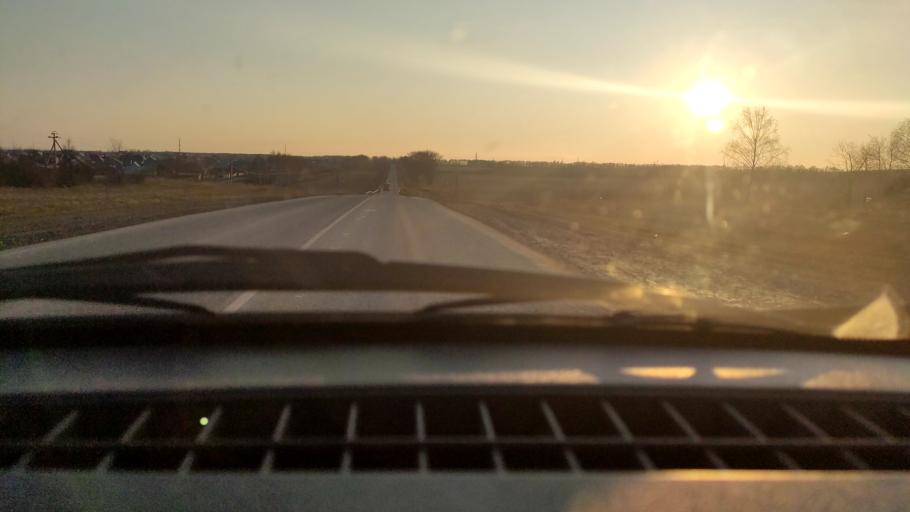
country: RU
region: Bashkortostan
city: Davlekanovo
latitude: 54.2371
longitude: 55.0410
